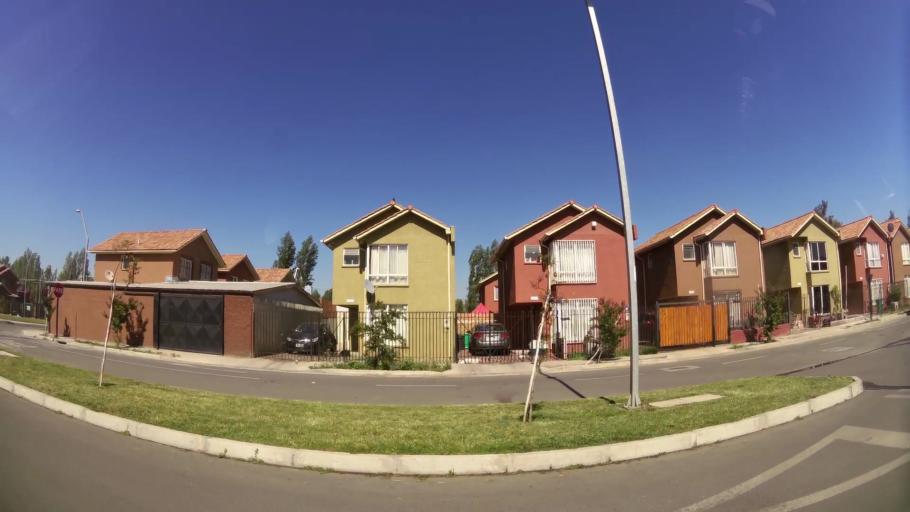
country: CL
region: Santiago Metropolitan
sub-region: Provincia de Maipo
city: San Bernardo
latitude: -33.6141
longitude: -70.6821
